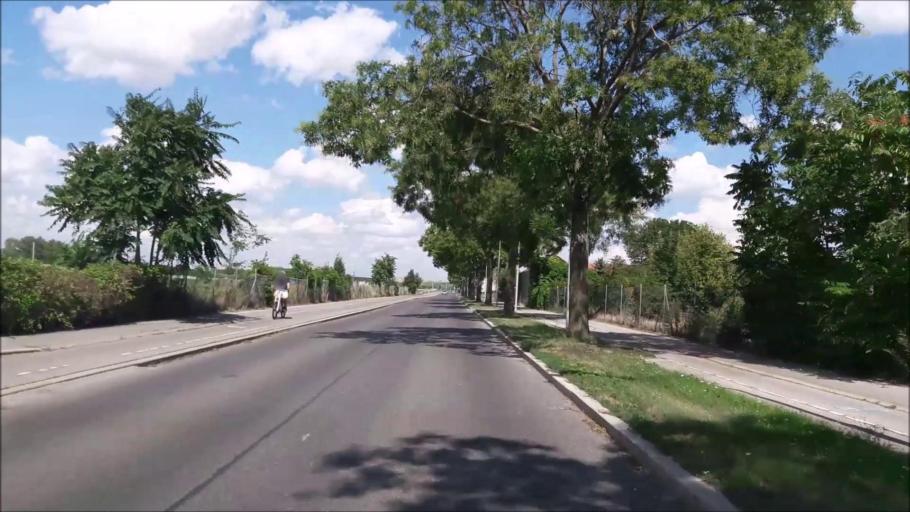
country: AT
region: Lower Austria
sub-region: Politischer Bezirk Wien-Umgebung
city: Gerasdorf bei Wien
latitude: 48.2398
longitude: 16.4658
